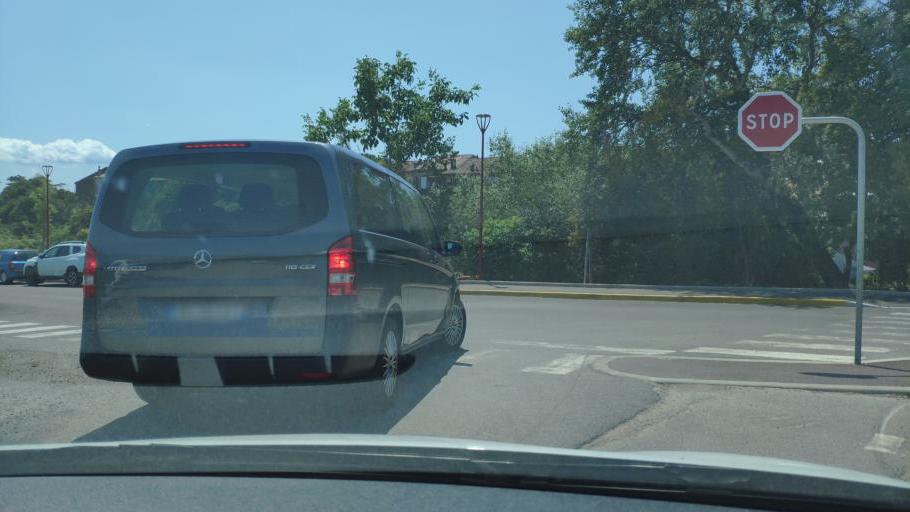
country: FR
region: Provence-Alpes-Cote d'Azur
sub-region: Departement du Var
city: Les Arcs
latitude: 43.4628
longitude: 6.4805
